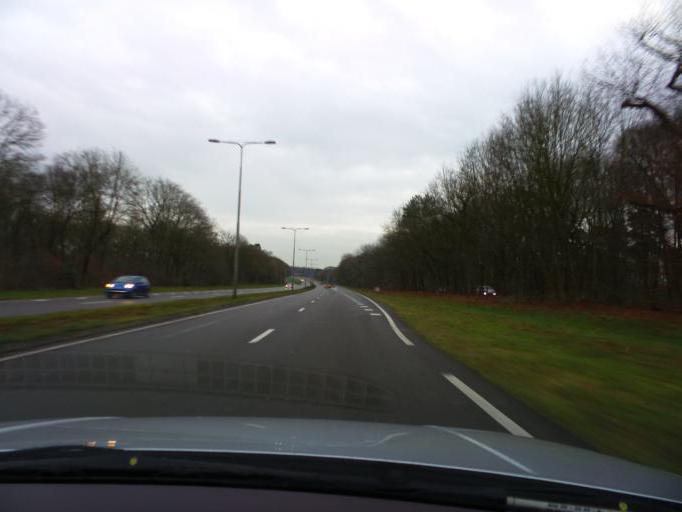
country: NL
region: Utrecht
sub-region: Gemeente Amersfoort
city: Amersfoort
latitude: 52.1346
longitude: 5.3681
